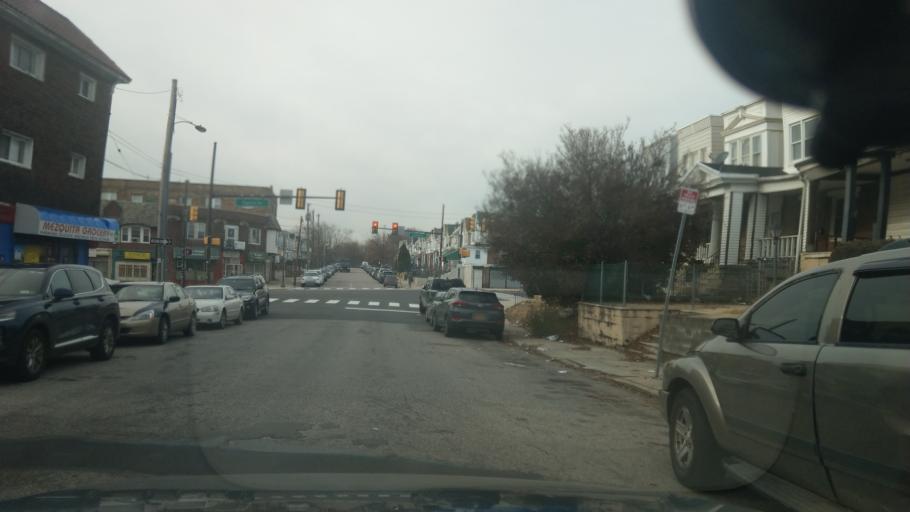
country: US
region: Pennsylvania
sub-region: Montgomery County
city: Wyncote
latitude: 40.0450
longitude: -75.1490
